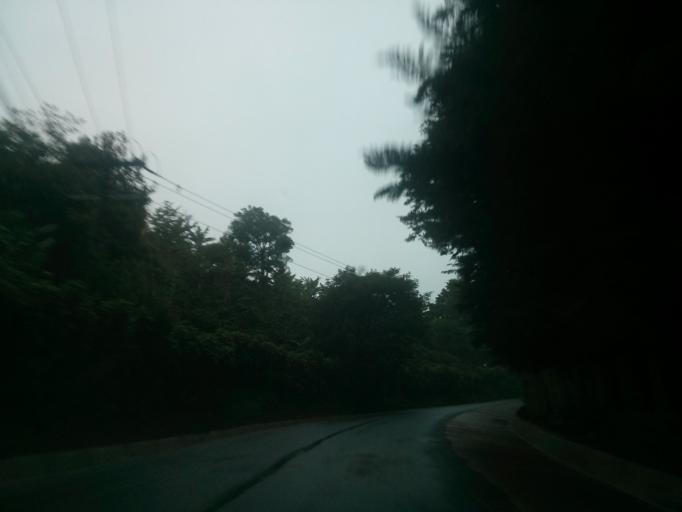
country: CR
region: Alajuela
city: Sabanilla
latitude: 10.0968
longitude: -84.1921
